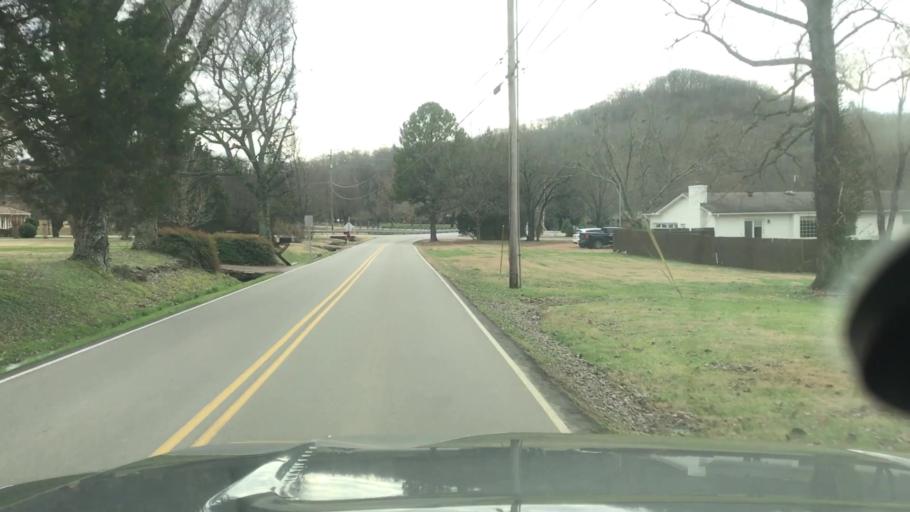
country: US
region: Tennessee
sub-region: Davidson County
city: Forest Hills
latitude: 36.0265
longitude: -86.8492
